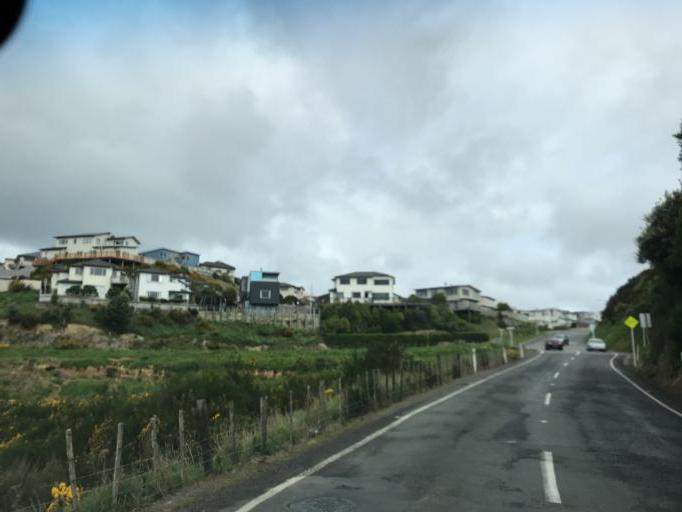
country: NZ
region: Wellington
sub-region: Wellington City
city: Kelburn
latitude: -41.2142
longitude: 174.7960
